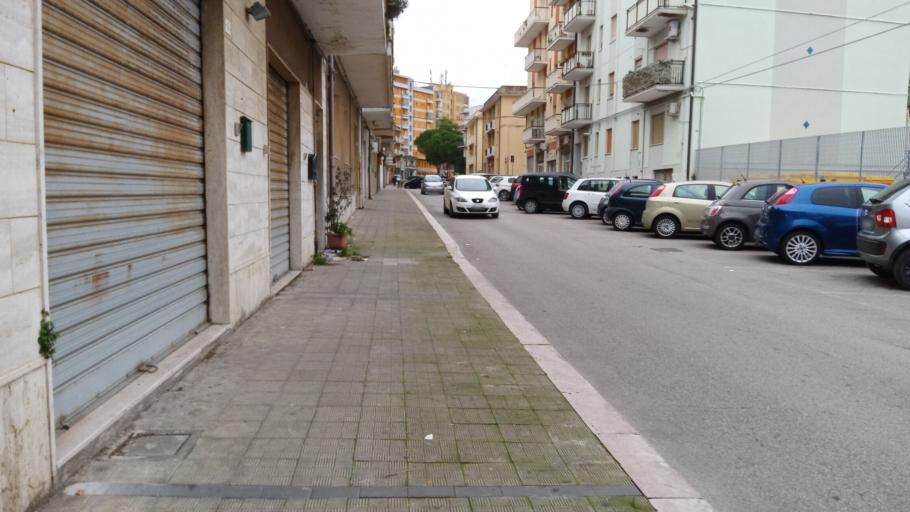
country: IT
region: Molise
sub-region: Provincia di Campobasso
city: Termoli
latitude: 42.0004
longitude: 14.9915
